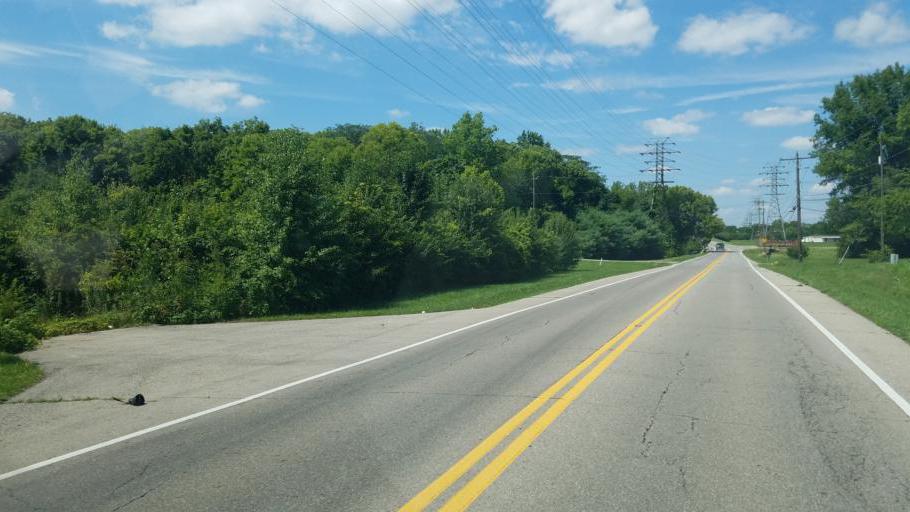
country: US
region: Ohio
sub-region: Franklin County
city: Obetz
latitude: 39.8686
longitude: -82.9888
